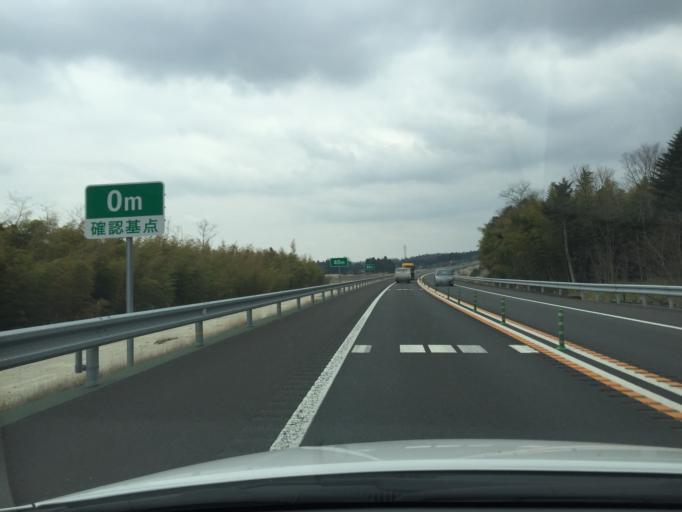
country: JP
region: Miyagi
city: Marumori
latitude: 37.8083
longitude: 140.8837
